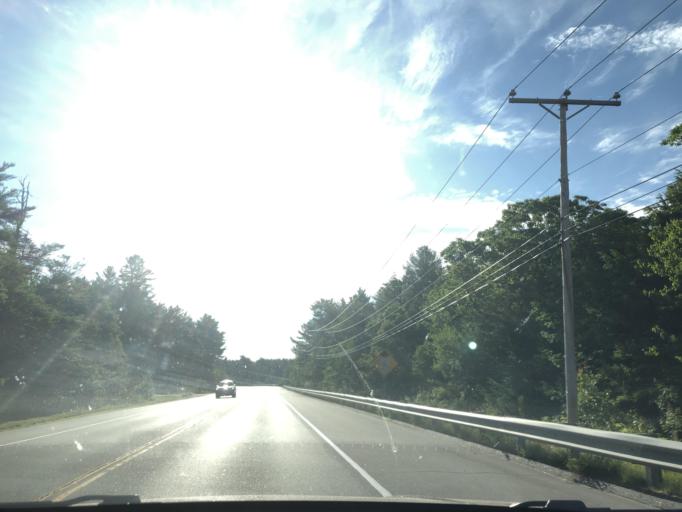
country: US
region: New Hampshire
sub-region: Merrimack County
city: New London
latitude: 43.3941
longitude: -71.9715
